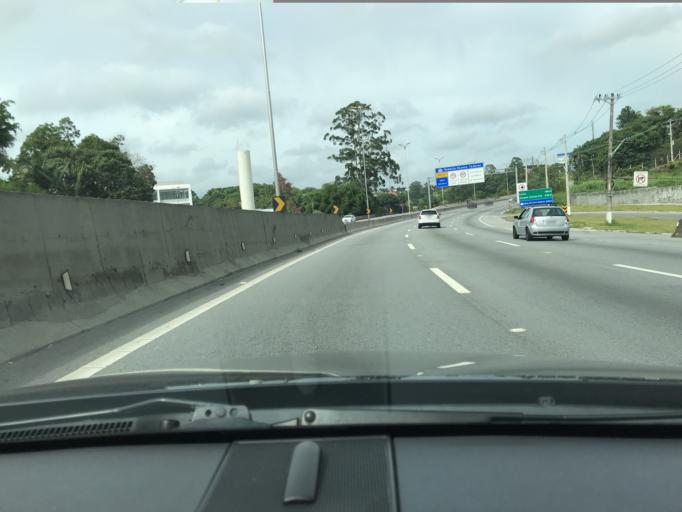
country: BR
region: Sao Paulo
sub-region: Taboao Da Serra
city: Taboao da Serra
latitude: -23.5910
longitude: -46.8184
